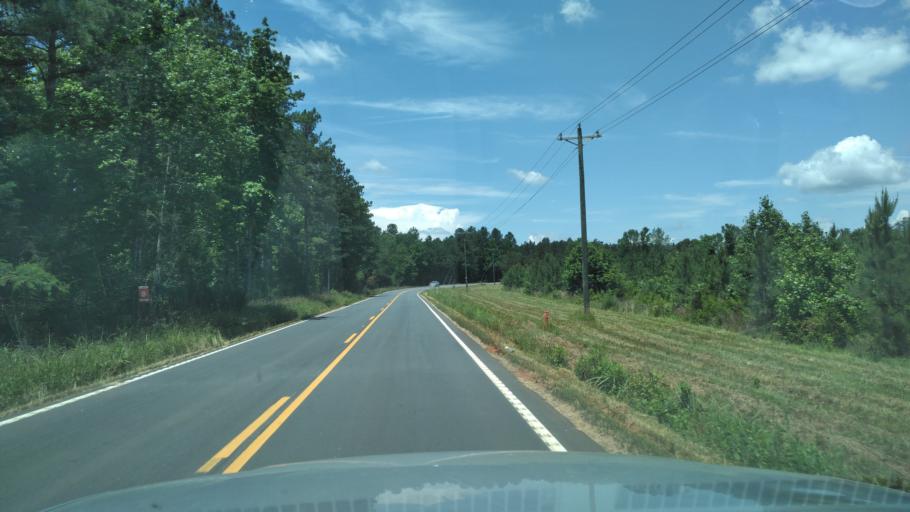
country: US
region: South Carolina
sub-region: Greenwood County
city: Ware Shoals
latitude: 34.3893
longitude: -82.1172
